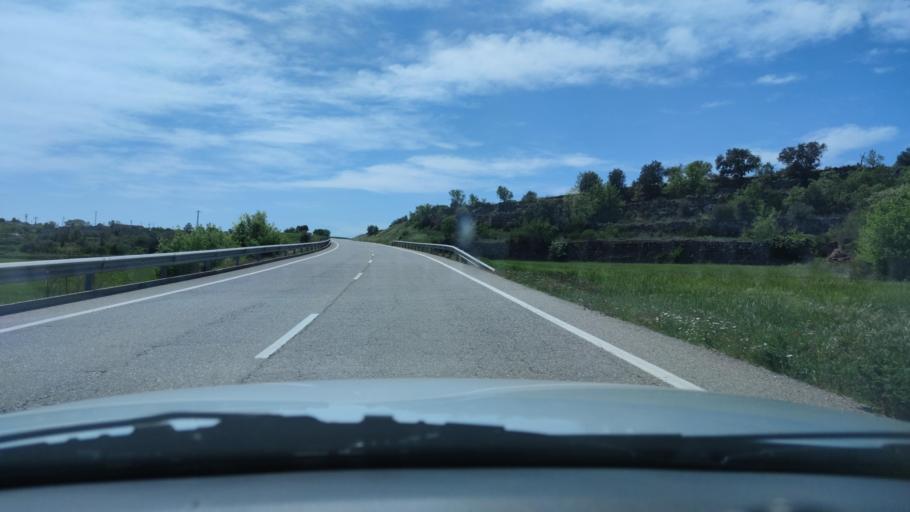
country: ES
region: Catalonia
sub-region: Provincia de Lleida
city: Tora de Riubregos
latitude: 41.8049
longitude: 1.3104
